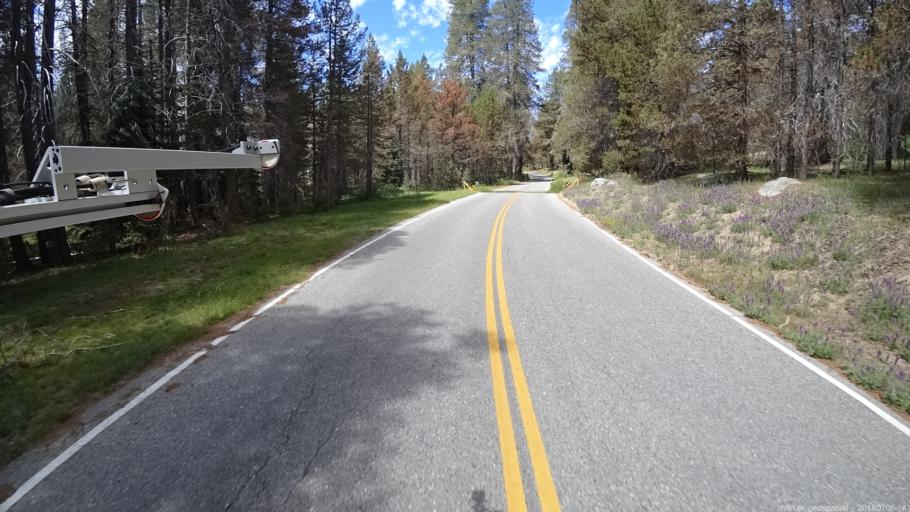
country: US
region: California
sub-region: Madera County
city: Oakhurst
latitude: 37.4472
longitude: -119.4542
